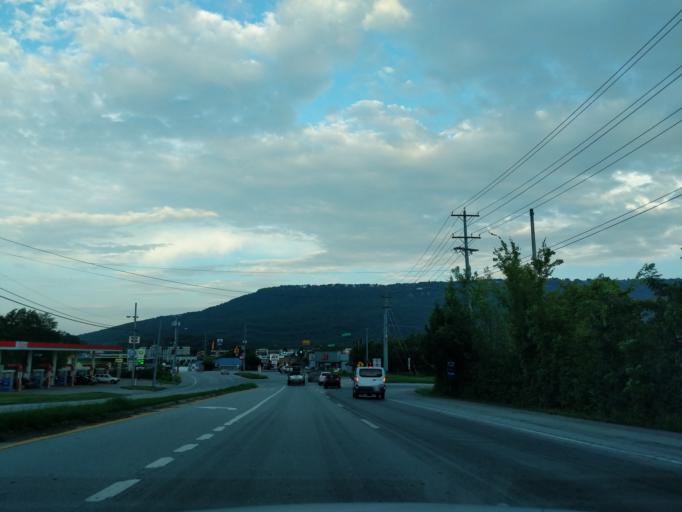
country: US
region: Tennessee
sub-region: Hamilton County
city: Lookout Mountain
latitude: 35.0183
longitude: -85.3820
